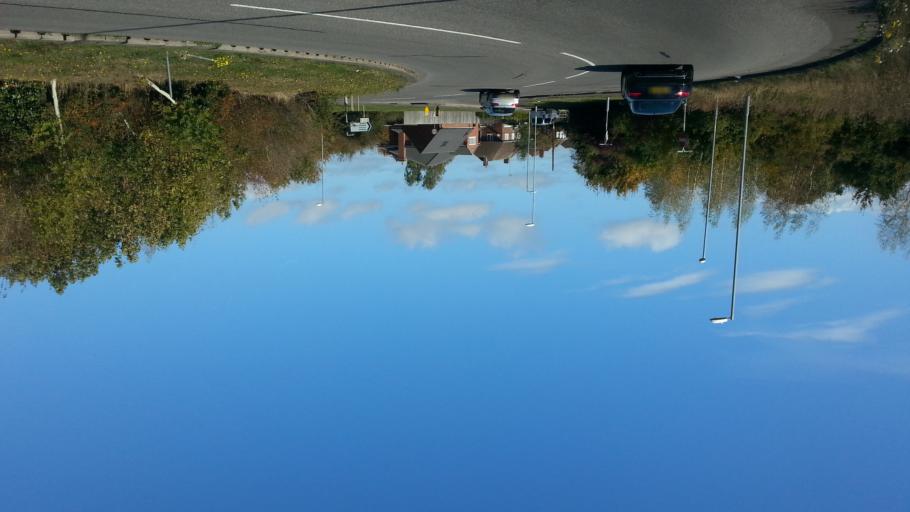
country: GB
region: England
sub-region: Northamptonshire
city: Higham Ferrers
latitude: 52.3088
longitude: -0.5850
